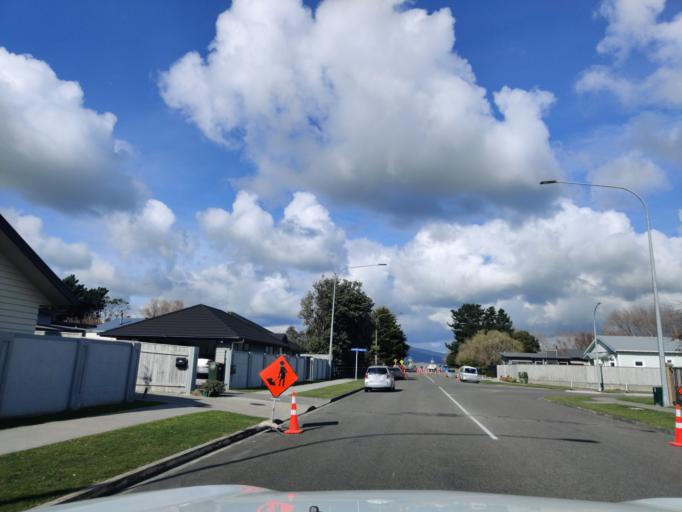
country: NZ
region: Manawatu-Wanganui
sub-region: Palmerston North City
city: Palmerston North
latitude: -40.3271
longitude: 175.6633
